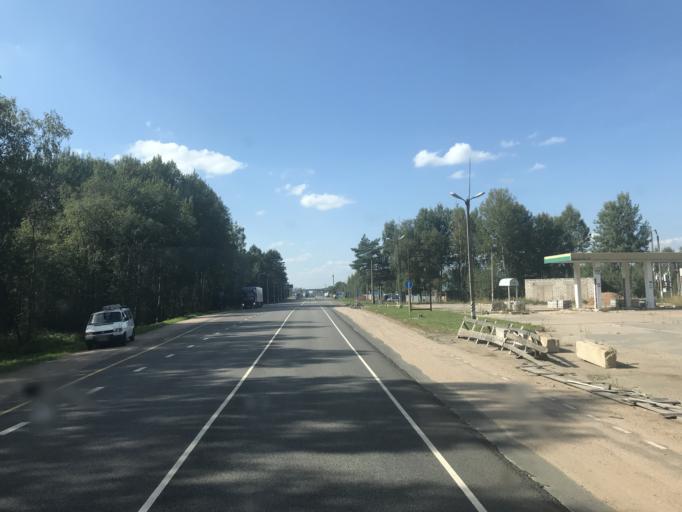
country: RU
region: Smolensk
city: Rudnya
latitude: 54.9859
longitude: 30.9619
